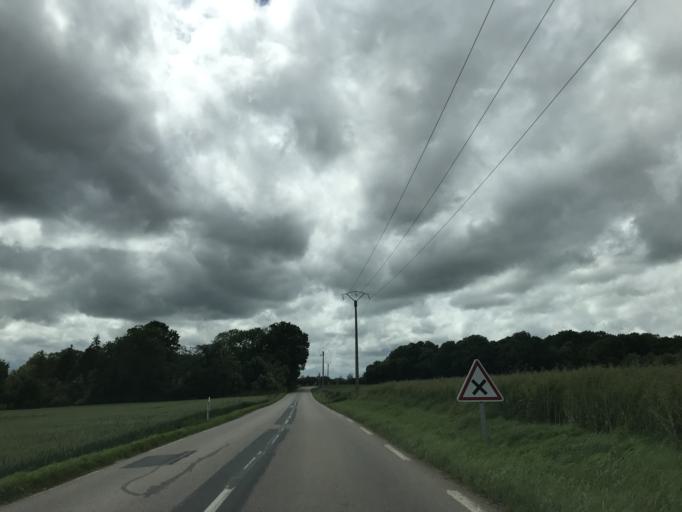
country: FR
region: Ile-de-France
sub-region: Departement des Yvelines
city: Longnes
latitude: 48.9744
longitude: 1.5800
